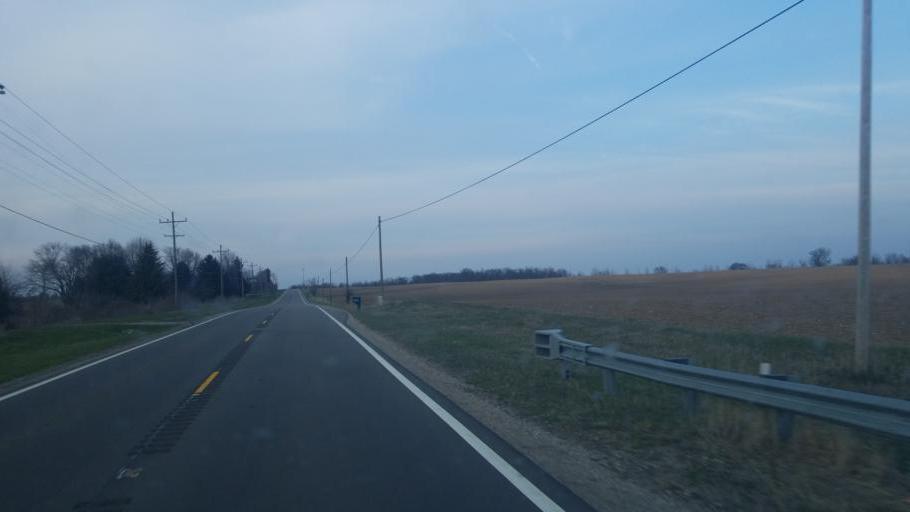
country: US
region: Ohio
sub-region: Marion County
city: Marion
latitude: 40.5255
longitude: -83.1633
